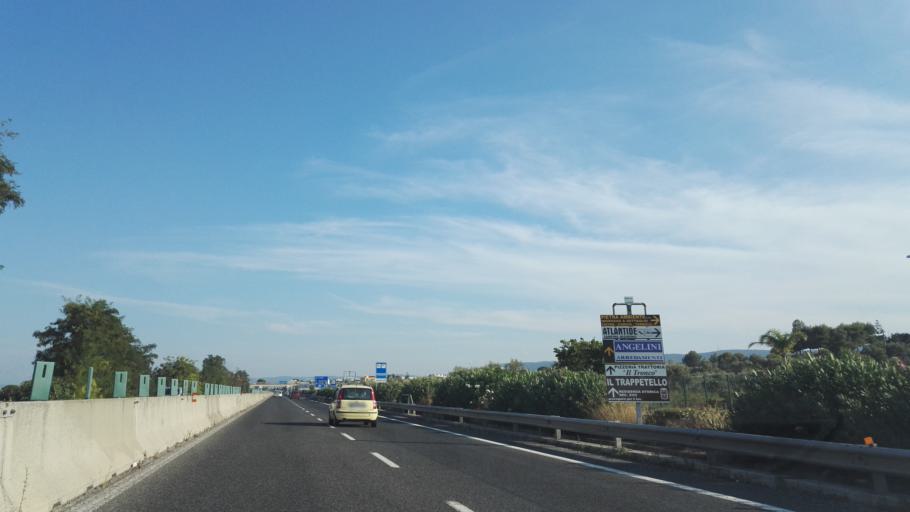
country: IT
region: Apulia
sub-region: Provincia di Bari
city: Monopoli
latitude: 40.8998
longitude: 17.3281
